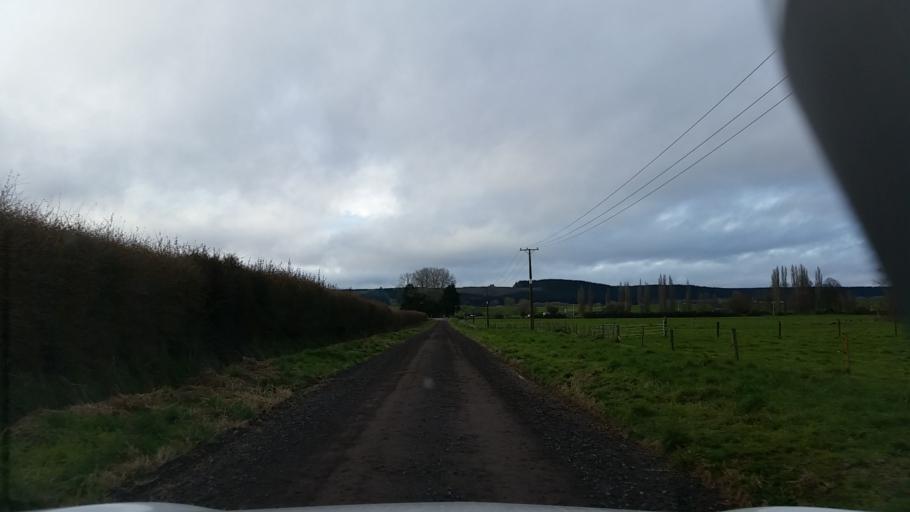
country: NZ
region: Bay of Plenty
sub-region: Rotorua District
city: Rotorua
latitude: -38.4069
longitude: 176.3736
